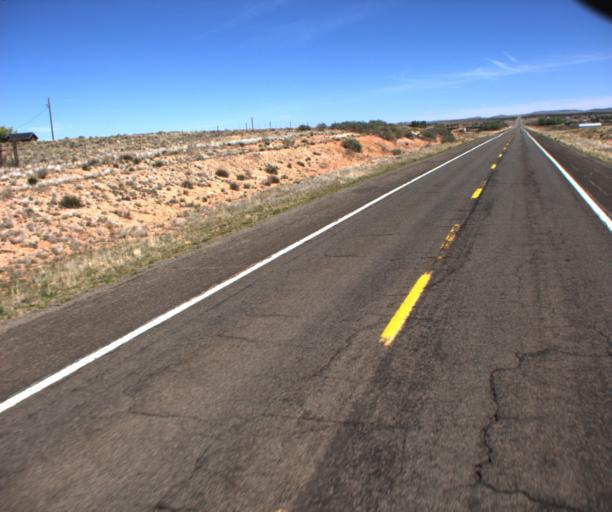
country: US
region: Arizona
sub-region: Mohave County
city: Peach Springs
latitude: 35.4799
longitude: -113.5736
